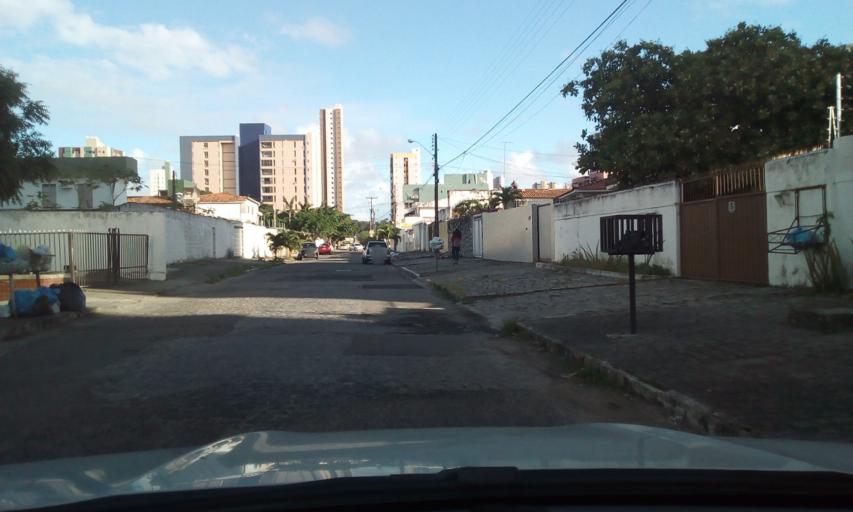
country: BR
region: Paraiba
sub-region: Joao Pessoa
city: Joao Pessoa
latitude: -7.1034
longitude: -34.8417
